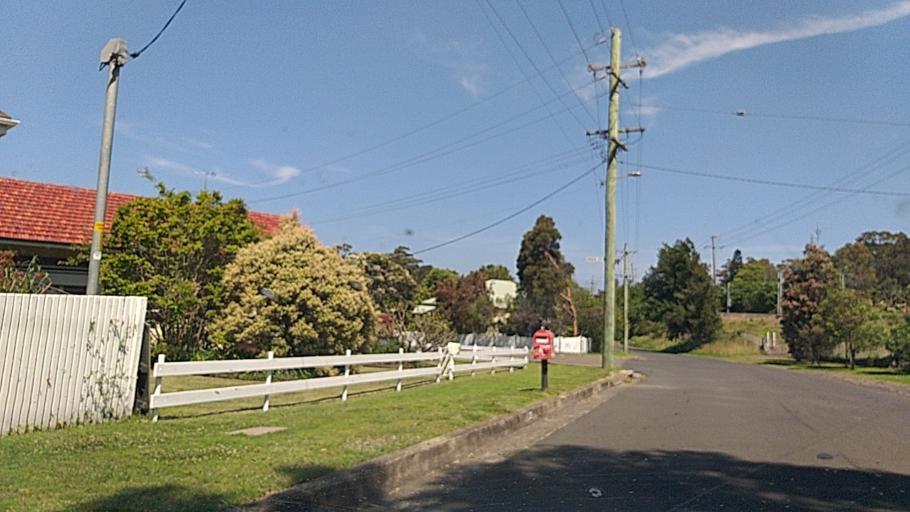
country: AU
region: New South Wales
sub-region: Wollongong
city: Bulli
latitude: -34.3396
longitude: 150.9141
